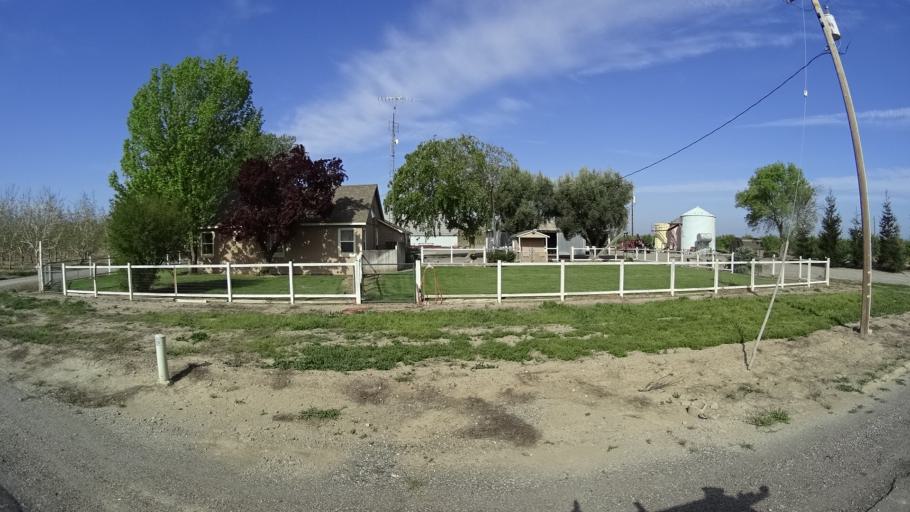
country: US
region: California
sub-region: Glenn County
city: Hamilton City
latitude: 39.6221
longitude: -122.0462
